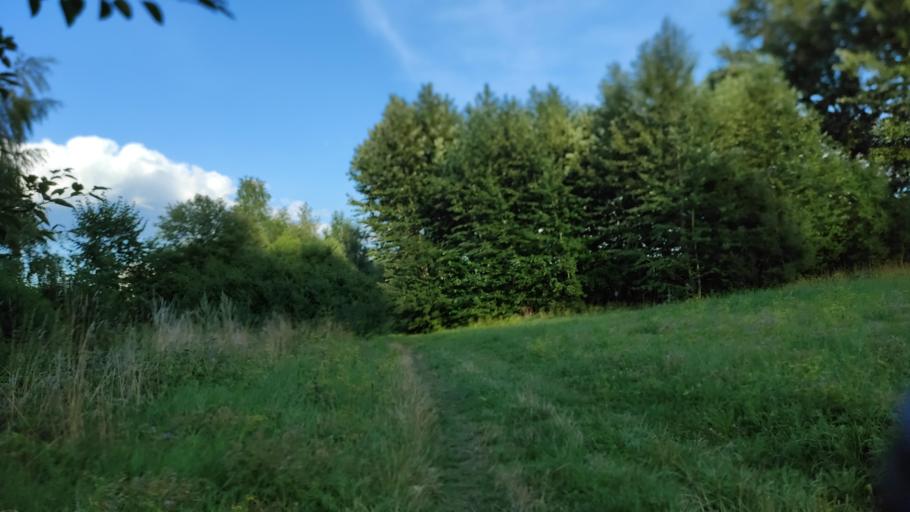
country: SK
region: Zilinsky
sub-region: Okres Liptovsky Mikulas
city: Liptovsky Mikulas
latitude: 49.0779
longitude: 19.5929
